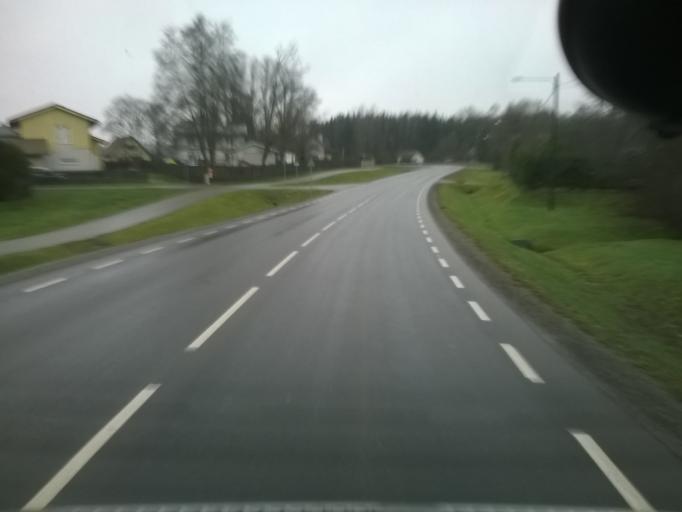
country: EE
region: Harju
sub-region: Saku vald
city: Saku
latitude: 59.2397
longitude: 24.6807
